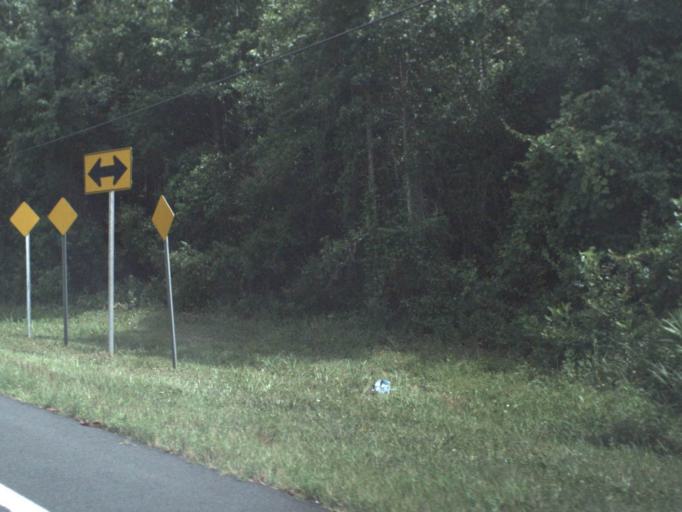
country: US
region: Florida
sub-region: Columbia County
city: Watertown
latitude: 30.1635
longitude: -82.5711
